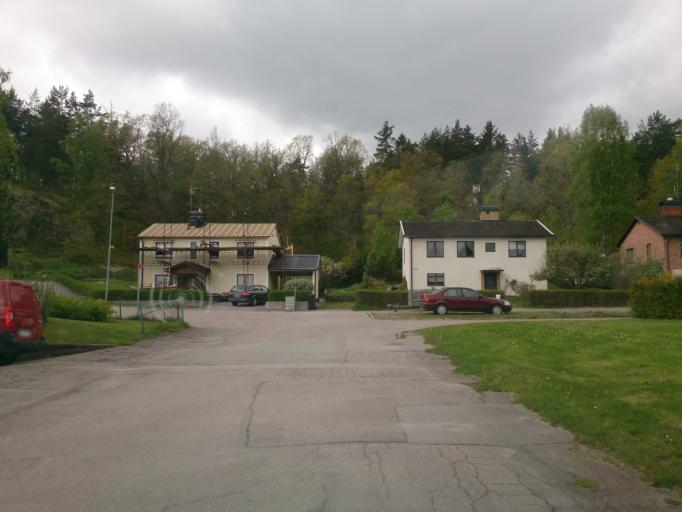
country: SE
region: OEstergoetland
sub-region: Atvidabergs Kommun
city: Atvidaberg
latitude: 58.2100
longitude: 16.0056
